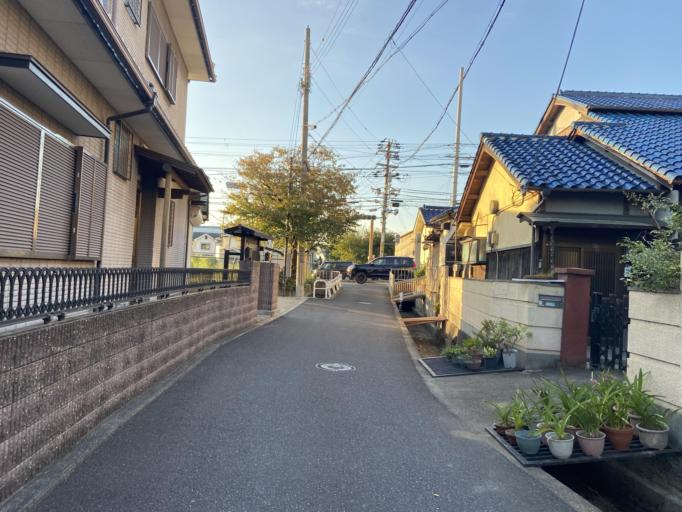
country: JP
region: Osaka
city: Kishiwada
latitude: 34.4428
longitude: 135.3817
